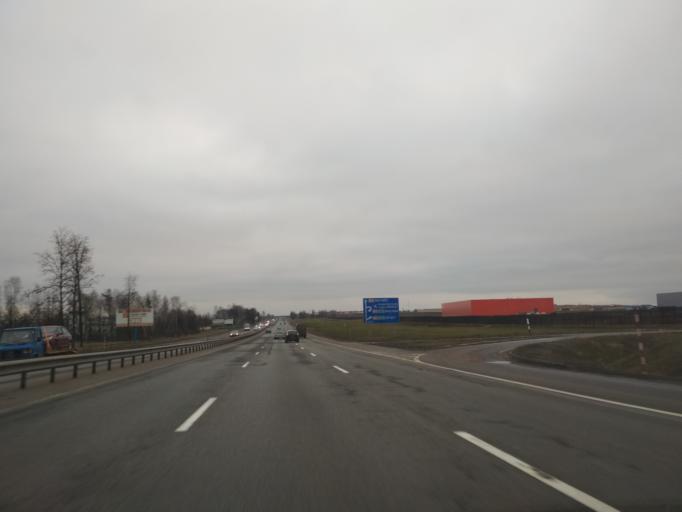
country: BY
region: Minsk
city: Pryvol'ny
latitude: 53.8117
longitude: 27.7787
